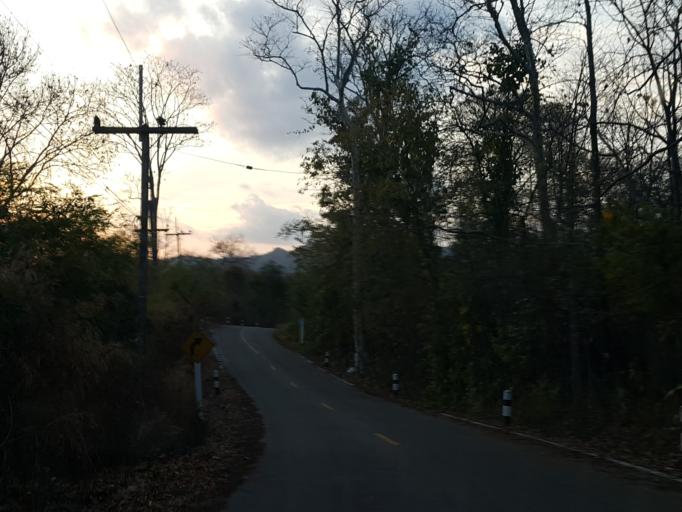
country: TH
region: Lampang
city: Mueang Pan
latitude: 18.8094
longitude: 99.4806
